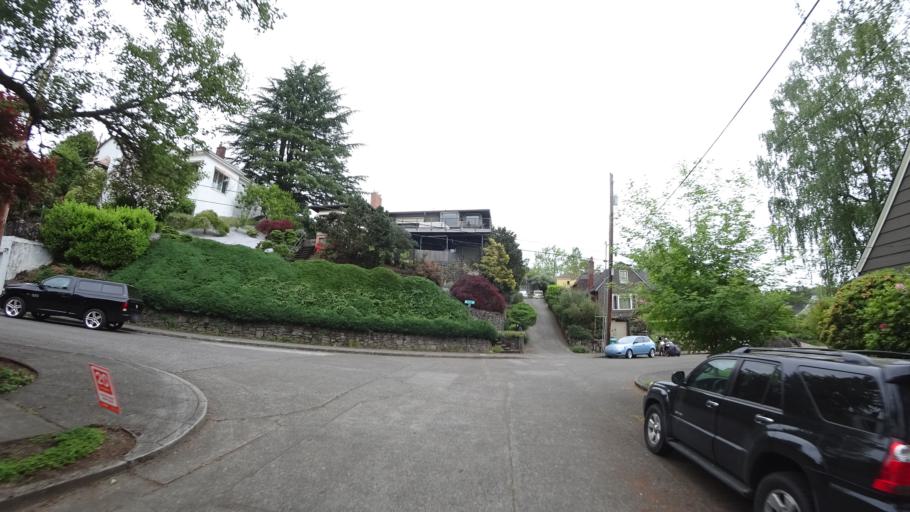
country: US
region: Oregon
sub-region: Multnomah County
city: Portland
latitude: 45.5454
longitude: -122.6267
